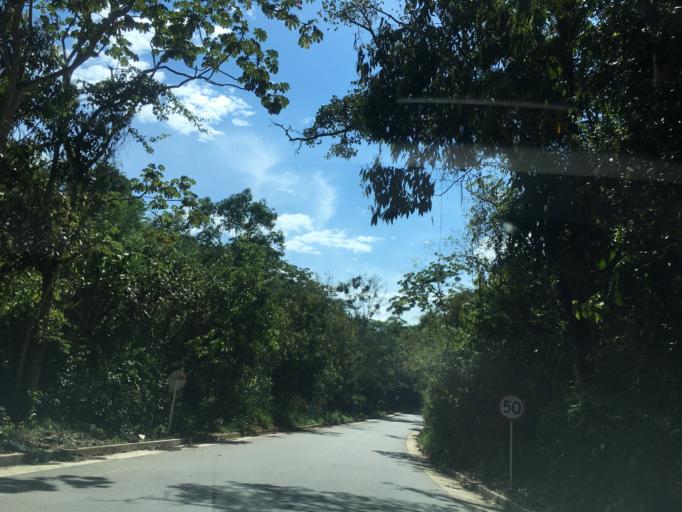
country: CO
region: Santander
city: Coromoro
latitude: 6.2909
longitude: -73.1485
